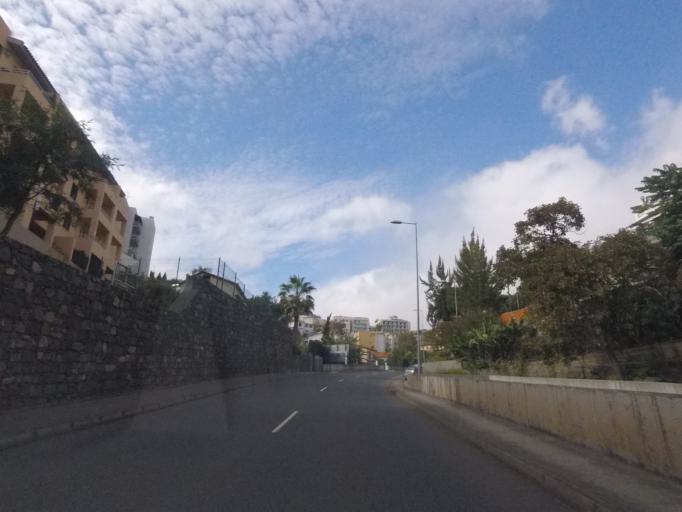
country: PT
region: Madeira
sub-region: Funchal
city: Funchal
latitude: 32.6480
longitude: -16.9254
